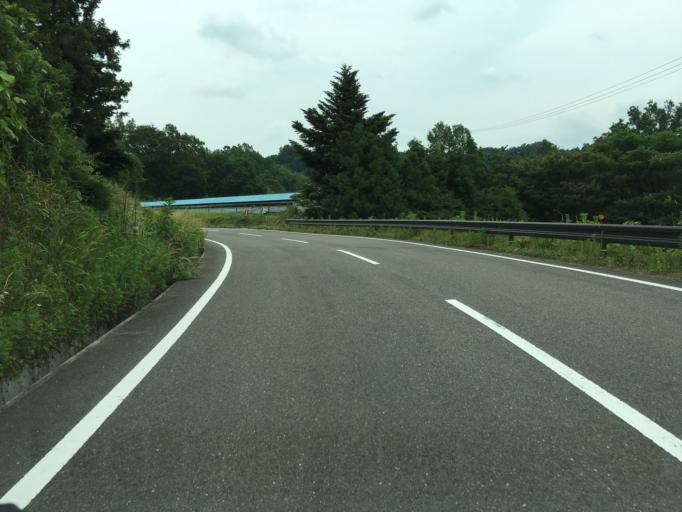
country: JP
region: Fukushima
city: Nihommatsu
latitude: 37.6296
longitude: 140.5369
